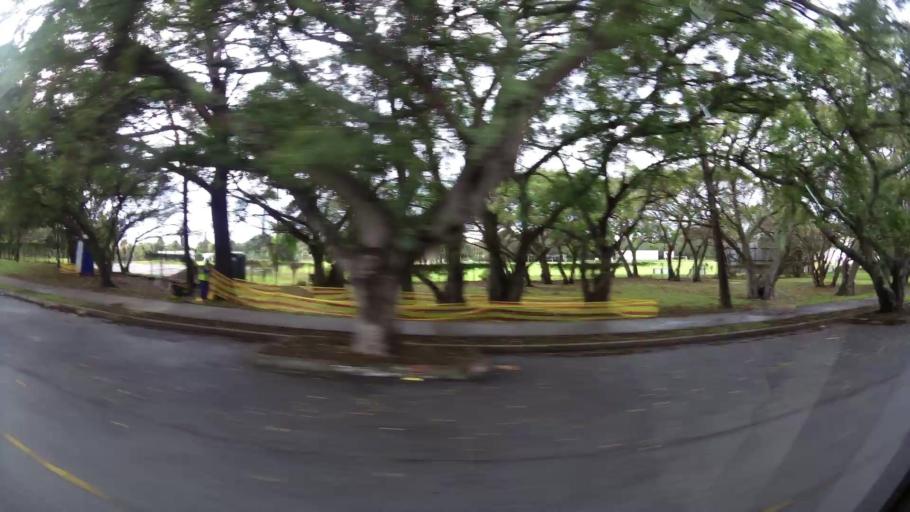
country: ZA
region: Eastern Cape
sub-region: Nelson Mandela Bay Metropolitan Municipality
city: Port Elizabeth
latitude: -33.9643
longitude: 25.6038
